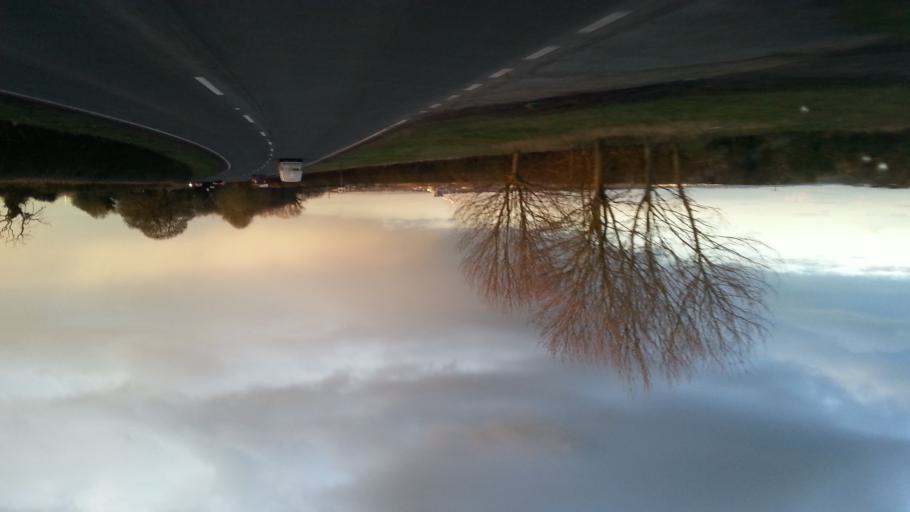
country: GB
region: England
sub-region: Nottinghamshire
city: Newark on Trent
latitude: 53.1103
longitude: -0.8573
